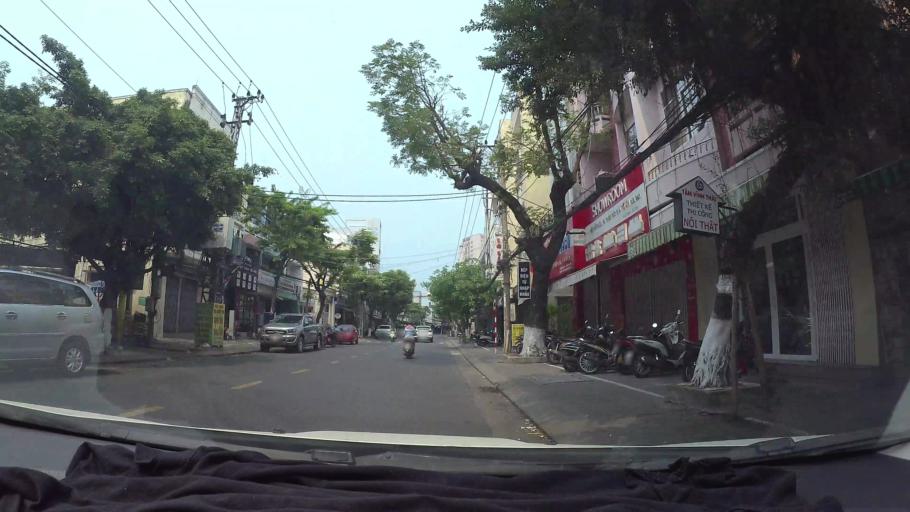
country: VN
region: Da Nang
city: Da Nang
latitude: 16.0583
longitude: 108.2209
